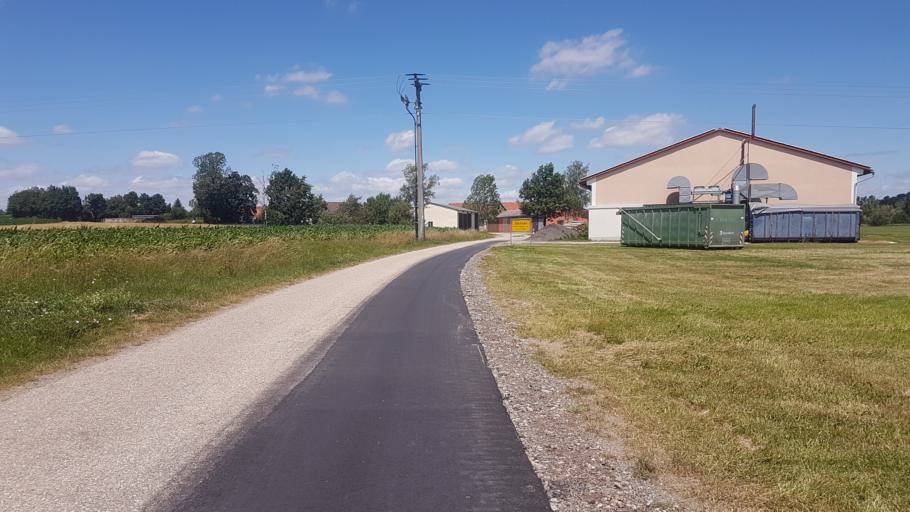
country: DE
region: Bavaria
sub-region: Regierungsbezirk Mittelfranken
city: Leutershausen
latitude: 49.2908
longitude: 10.4097
